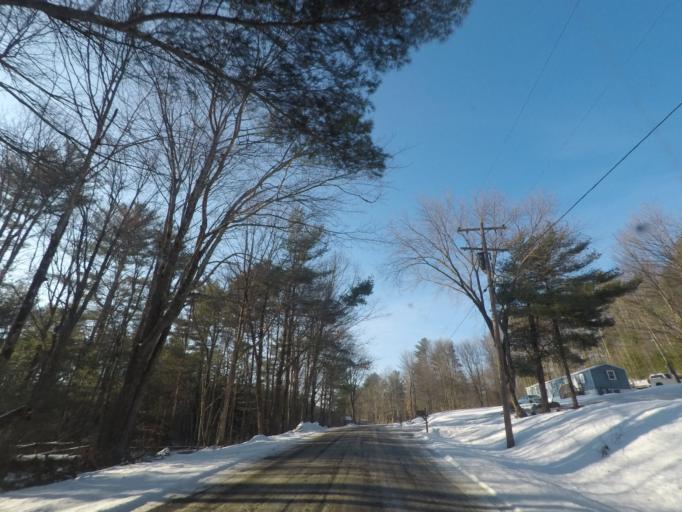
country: US
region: New York
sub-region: Rensselaer County
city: Nassau
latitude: 42.4980
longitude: -73.5025
